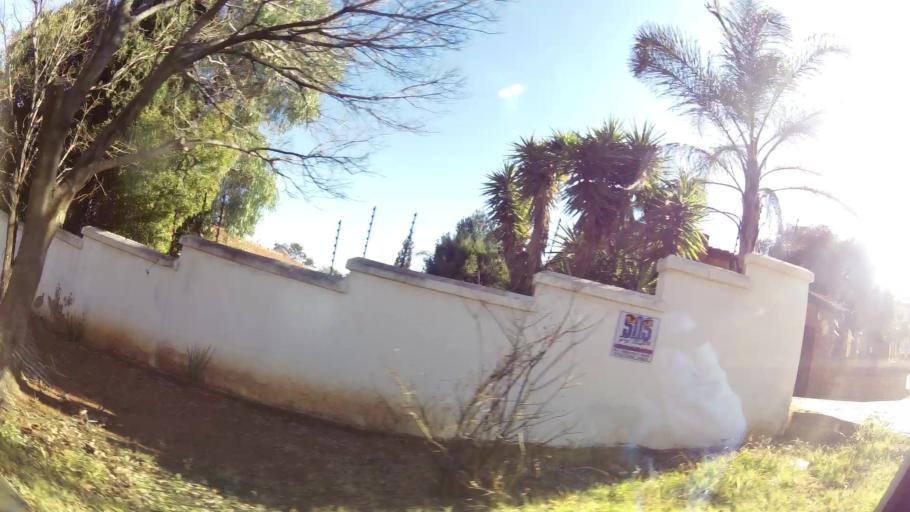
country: ZA
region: Gauteng
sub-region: City of Johannesburg Metropolitan Municipality
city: Johannesburg
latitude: -26.2852
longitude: 28.0520
